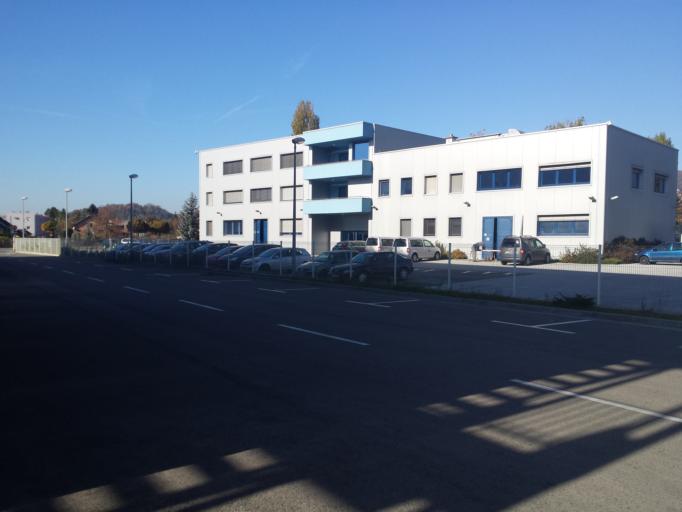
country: HR
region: Grad Zagreb
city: Jezdovec
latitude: 45.8118
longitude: 15.8470
